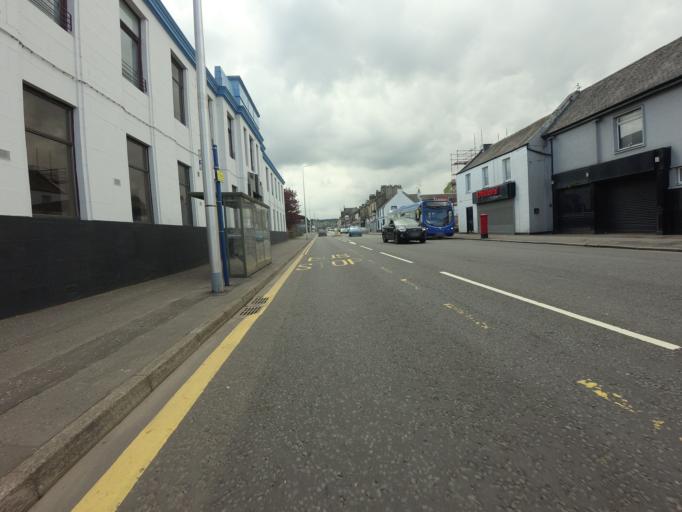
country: GB
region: Scotland
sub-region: Falkirk
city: Falkirk
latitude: 56.0101
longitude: -3.7851
